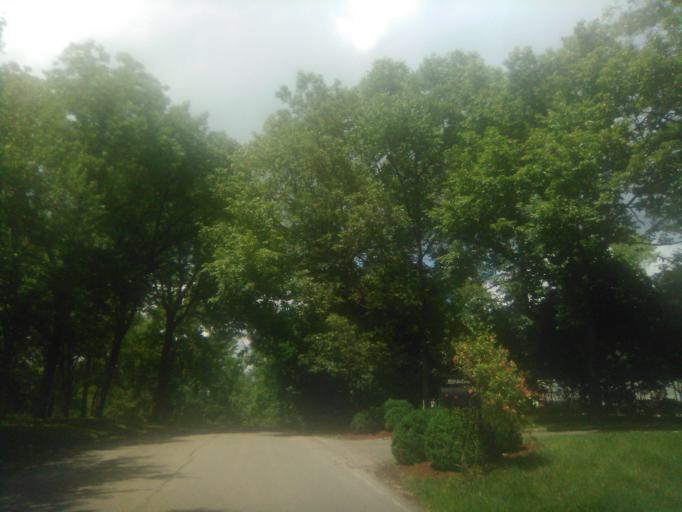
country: US
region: Tennessee
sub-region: Davidson County
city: Belle Meade
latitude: 36.1036
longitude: -86.8489
